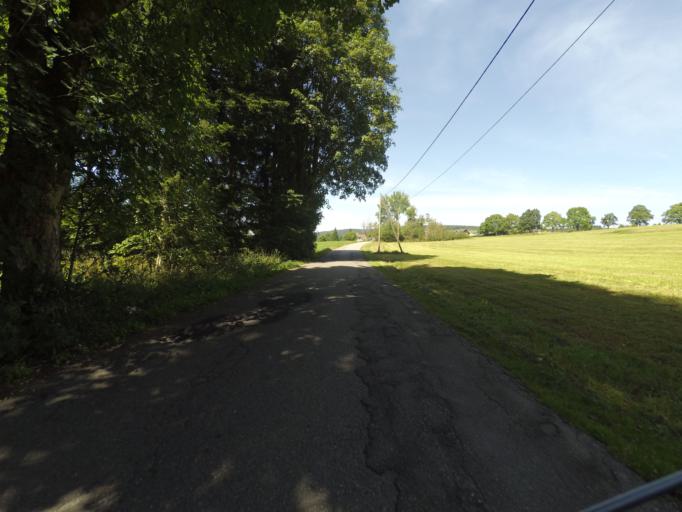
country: DE
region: Baden-Wuerttemberg
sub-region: Freiburg Region
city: Lenzkirch
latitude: 47.8670
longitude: 8.2402
